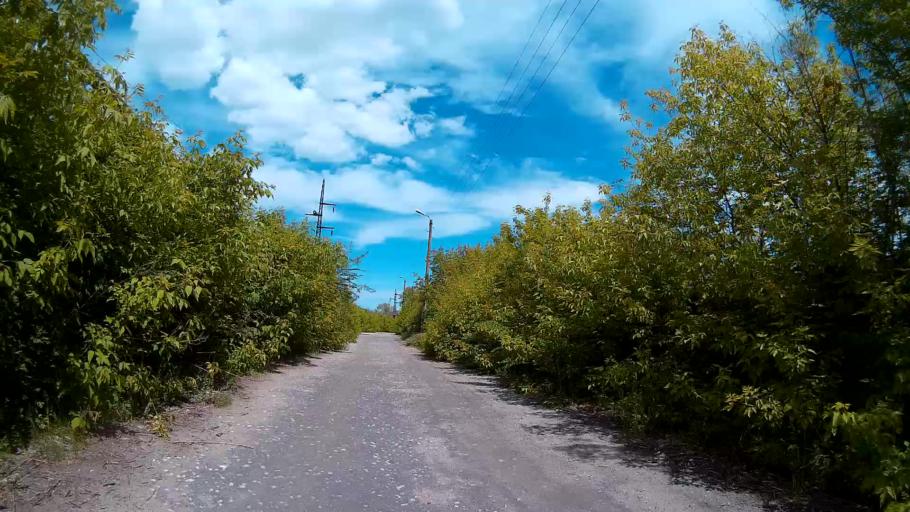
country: RU
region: Ulyanovsk
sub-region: Ulyanovskiy Rayon
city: Ulyanovsk
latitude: 54.2832
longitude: 48.3641
